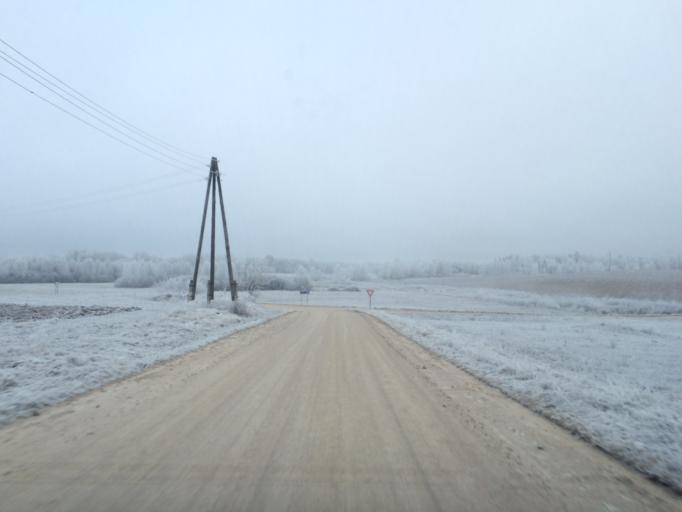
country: LV
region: Ludzas Rajons
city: Ludza
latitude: 56.6190
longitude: 27.5199
